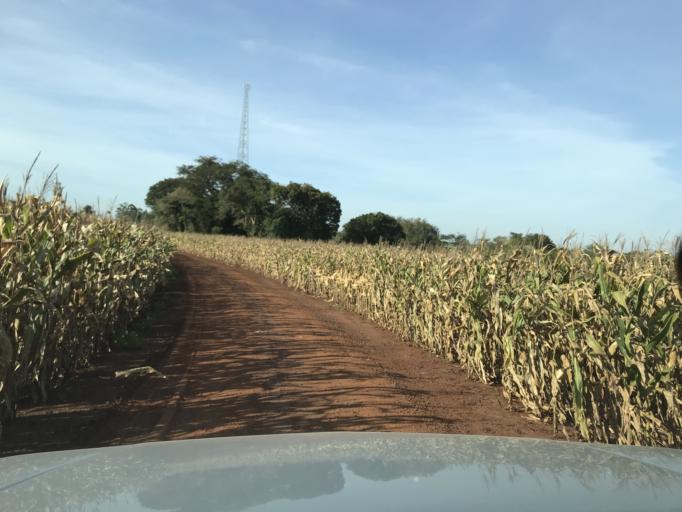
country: BR
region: Parana
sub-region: Palotina
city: Palotina
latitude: -24.2477
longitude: -53.7453
